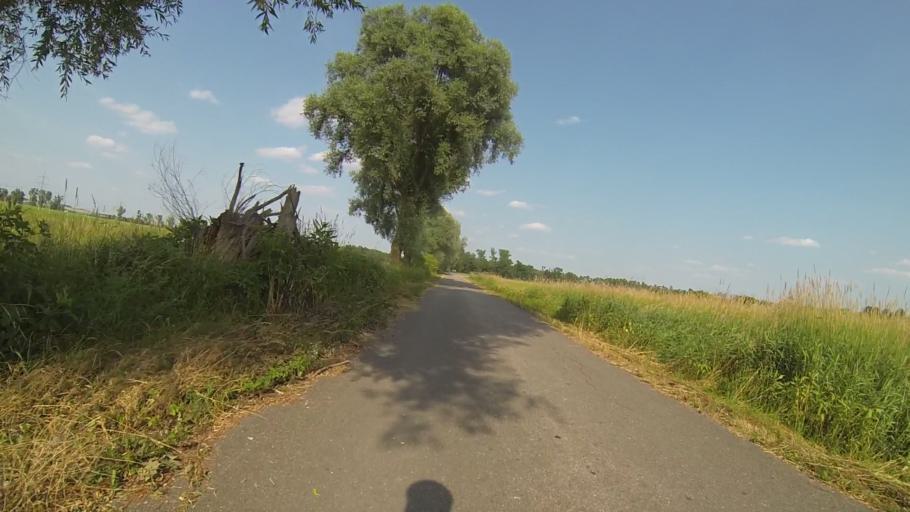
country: DE
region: Baden-Wuerttemberg
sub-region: Tuebingen Region
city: Rammingen
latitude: 48.4934
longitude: 10.1867
